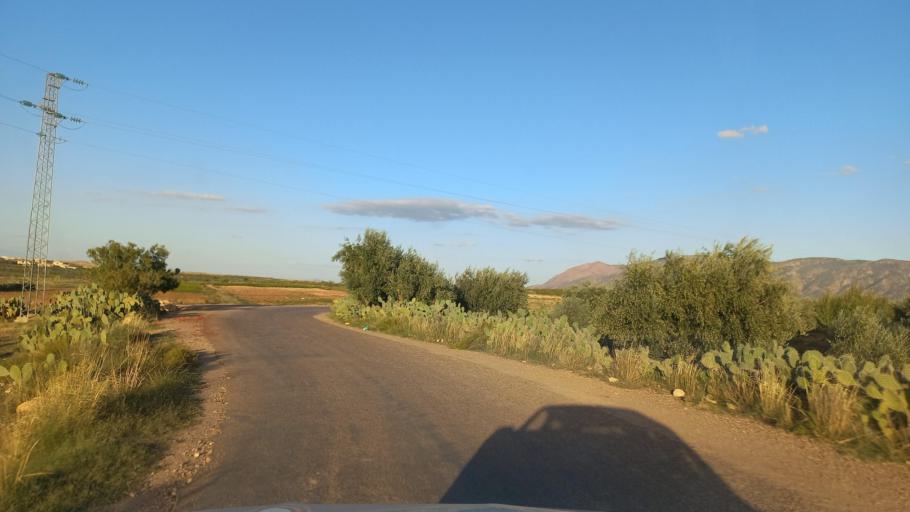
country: TN
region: Al Qasrayn
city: Sbiba
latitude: 35.4263
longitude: 9.1287
